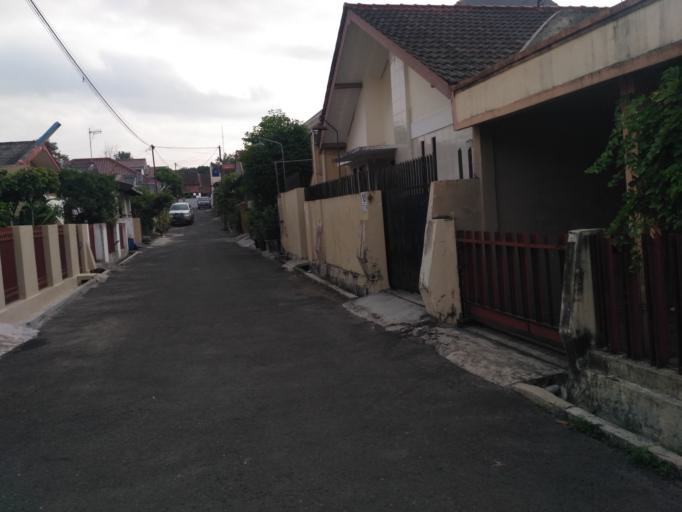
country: ID
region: Daerah Istimewa Yogyakarta
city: Melati
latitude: -7.7375
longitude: 110.3869
